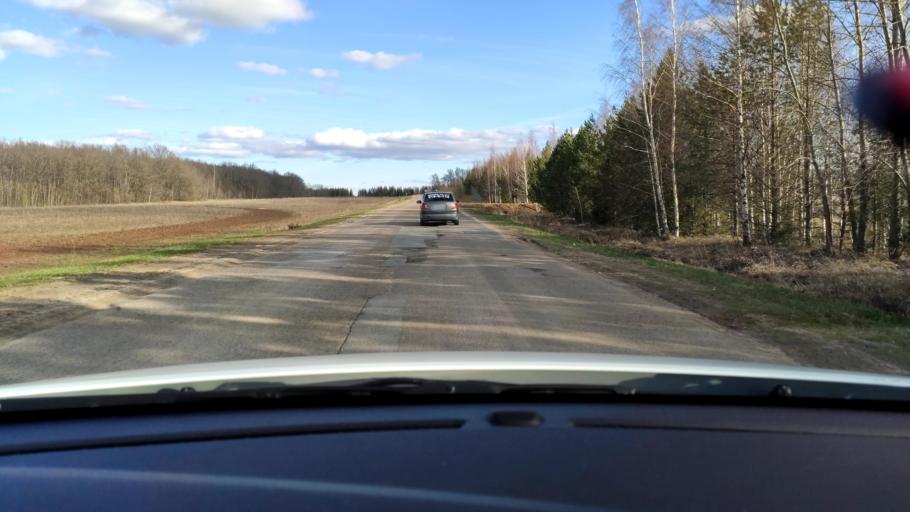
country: RU
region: Tatarstan
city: Vysokaya Gora
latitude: 55.8979
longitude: 49.3292
